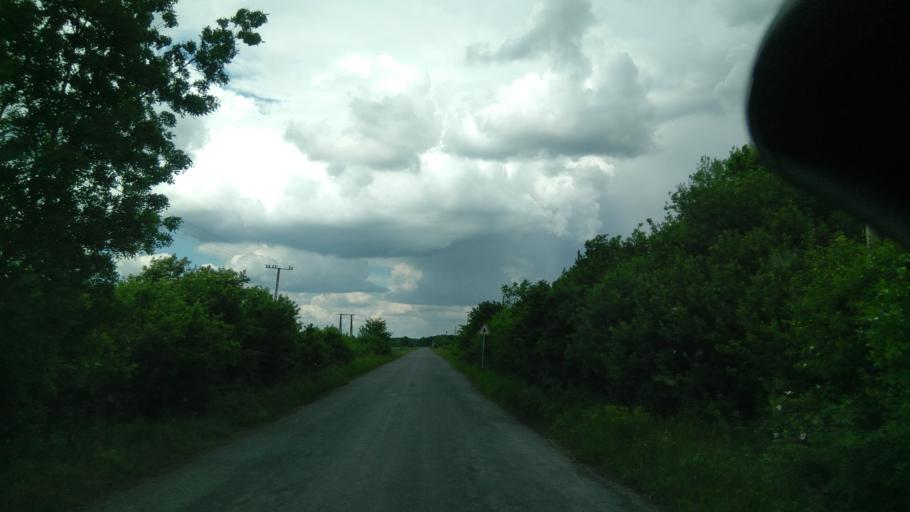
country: HU
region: Bekes
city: Szeghalom
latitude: 47.1024
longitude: 21.0793
